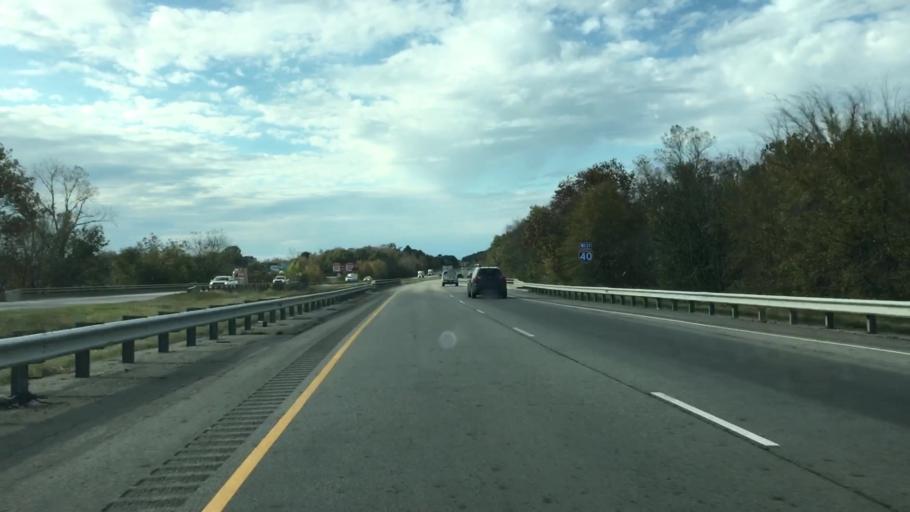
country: US
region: Arkansas
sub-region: Pope County
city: Pottsville
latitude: 35.2511
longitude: -93.0390
